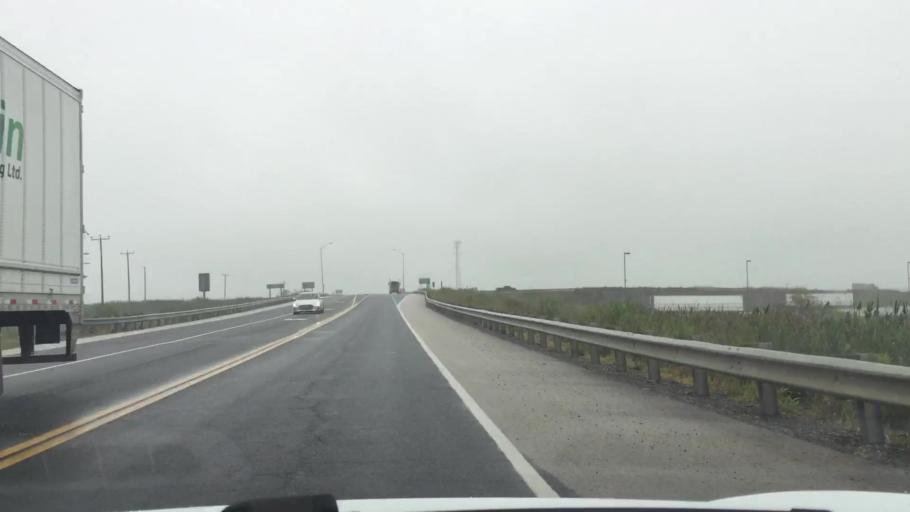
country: CA
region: Ontario
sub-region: Lambton County
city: Walpole Island
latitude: 42.2387
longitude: -82.5523
